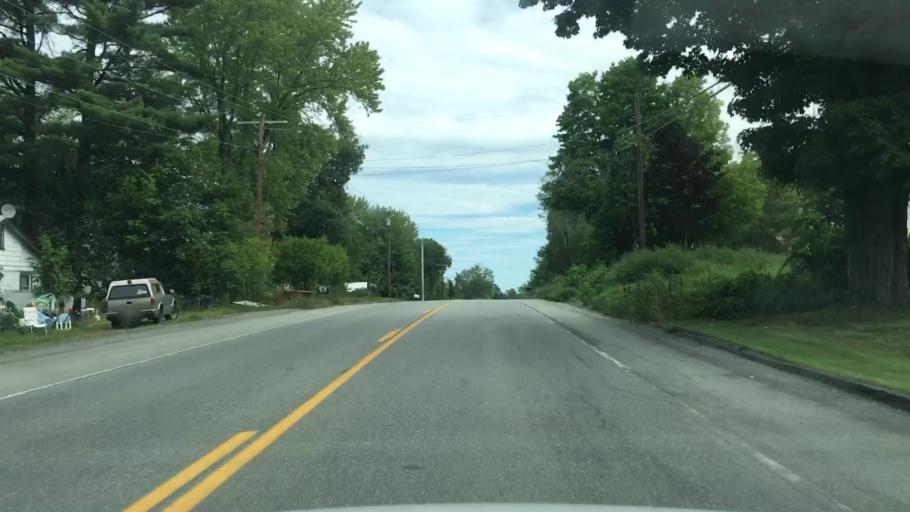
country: US
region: Maine
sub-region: Piscataquis County
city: Milo
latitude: 45.2469
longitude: -69.0016
